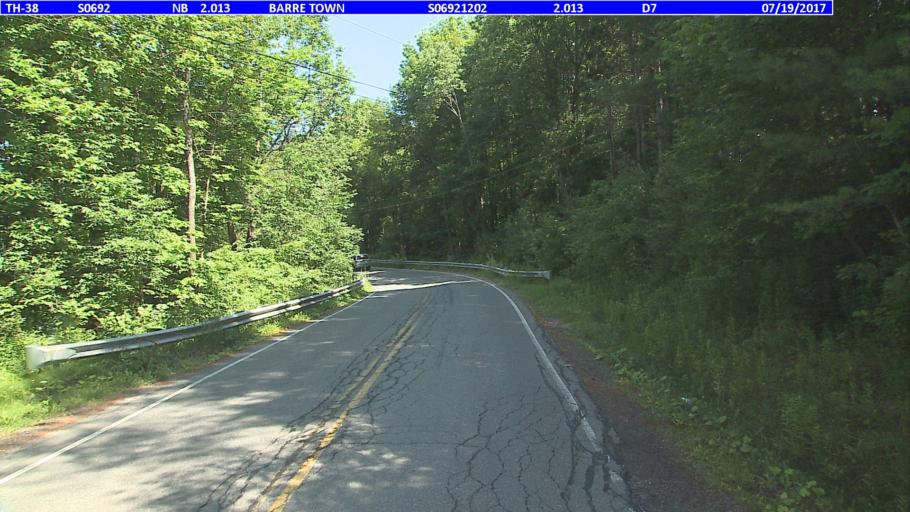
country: US
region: Vermont
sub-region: Washington County
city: Barre
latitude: 44.1846
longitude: -72.4657
